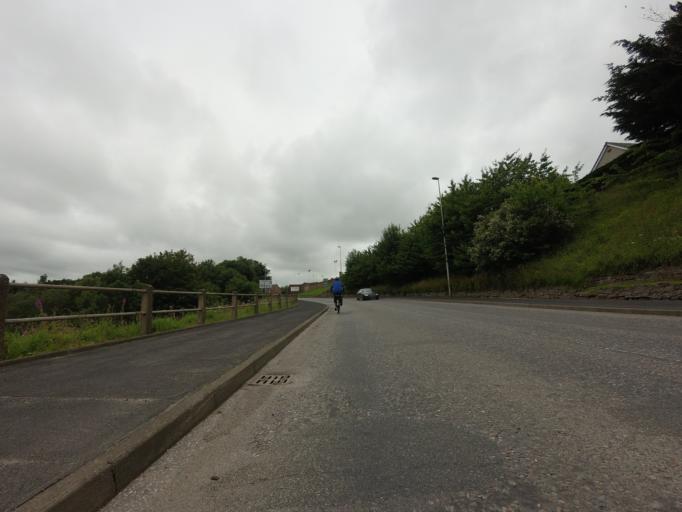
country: GB
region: Scotland
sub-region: Aberdeenshire
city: Turriff
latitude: 57.5362
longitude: -2.4632
